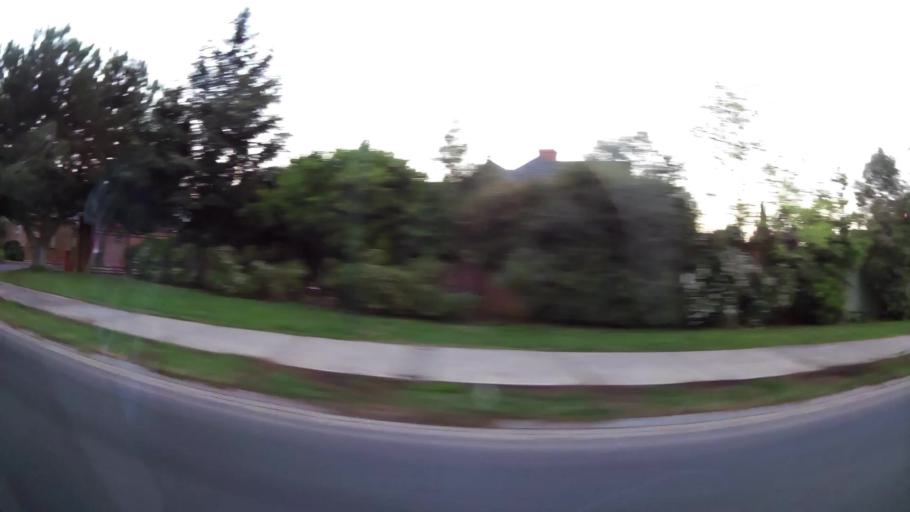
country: CL
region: Santiago Metropolitan
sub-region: Provincia de Chacabuco
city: Chicureo Abajo
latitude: -33.3295
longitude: -70.5427
